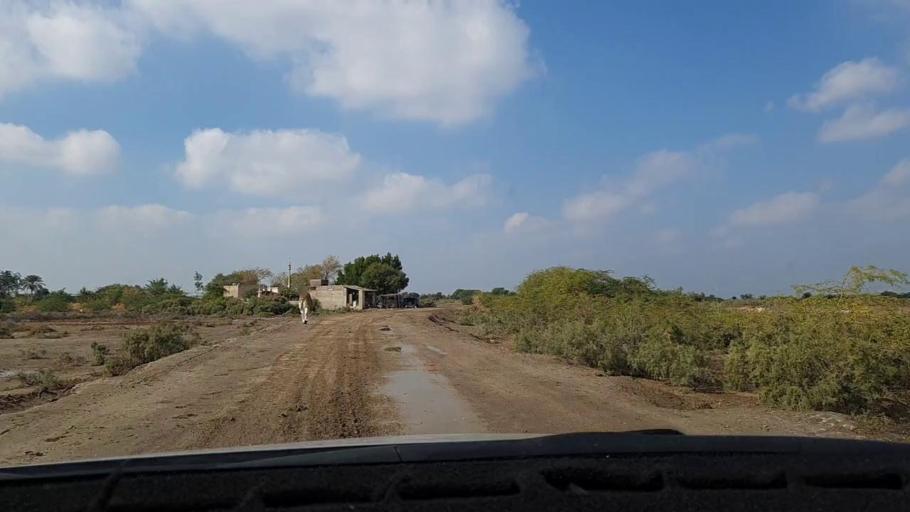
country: PK
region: Sindh
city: Tando Mittha Khan
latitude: 25.7739
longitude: 69.2586
